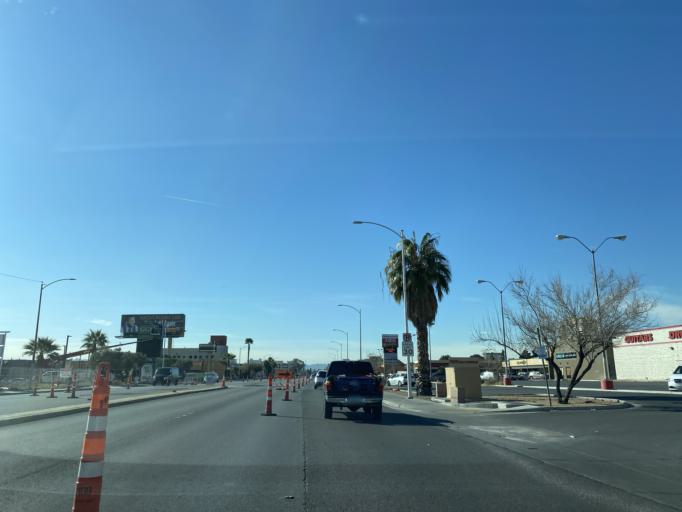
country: US
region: Nevada
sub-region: Clark County
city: Winchester
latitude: 36.1403
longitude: -115.1370
